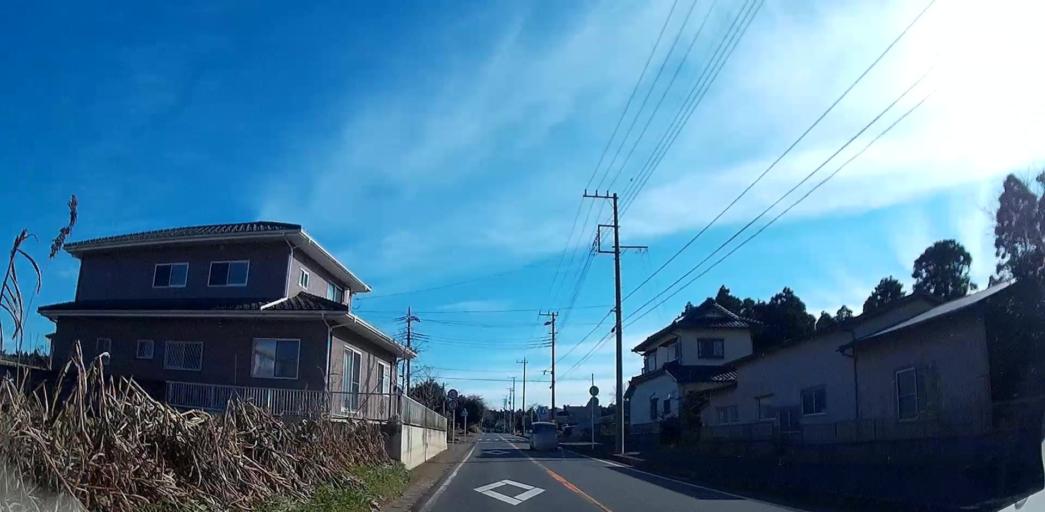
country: JP
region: Chiba
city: Yokaichiba
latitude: 35.7393
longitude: 140.4833
